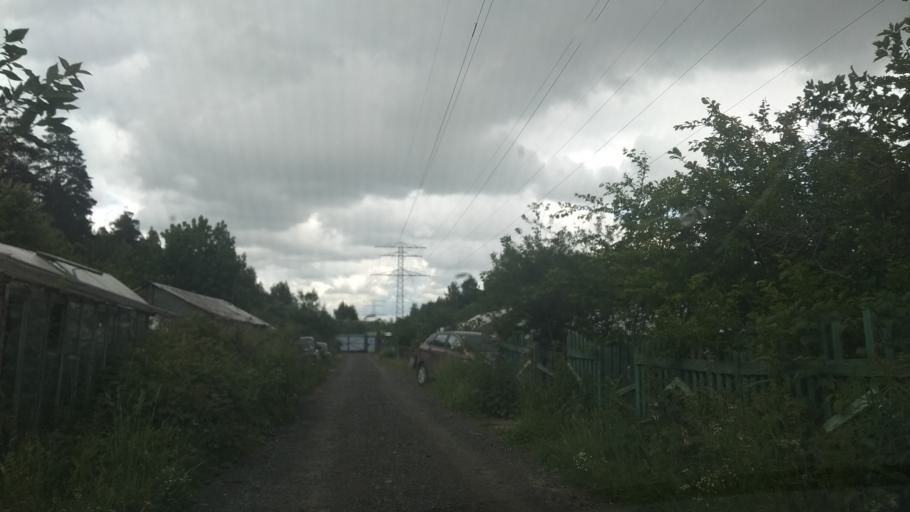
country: RU
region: Sverdlovsk
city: Verkhnyaya Pyshma
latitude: 56.9186
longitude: 60.5816
